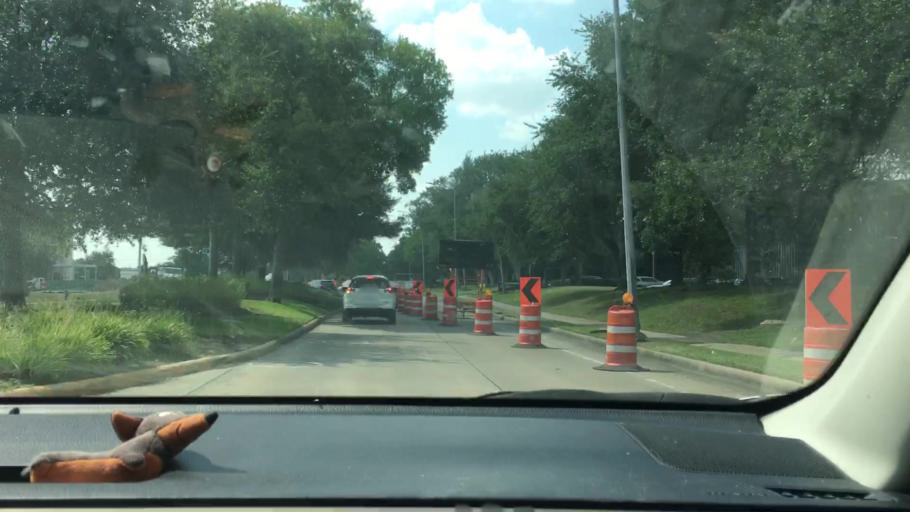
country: US
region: Texas
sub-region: Harris County
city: Bunker Hill Village
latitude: 29.7321
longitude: -95.5718
